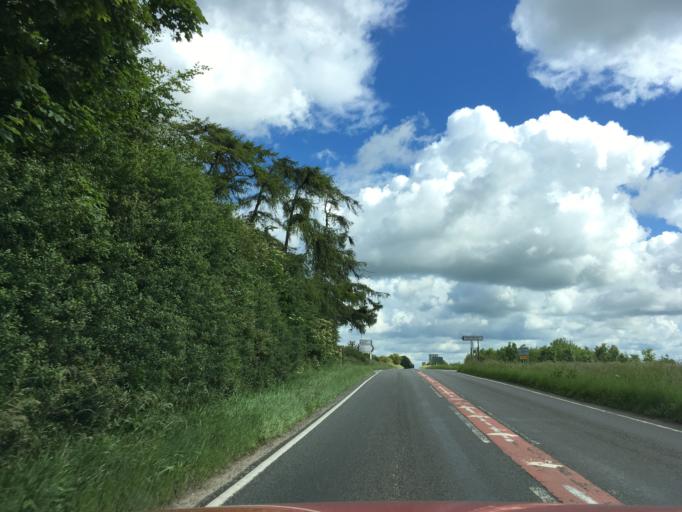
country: GB
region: England
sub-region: Oxfordshire
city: Shipton under Wychwood
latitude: 51.8370
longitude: -1.6057
